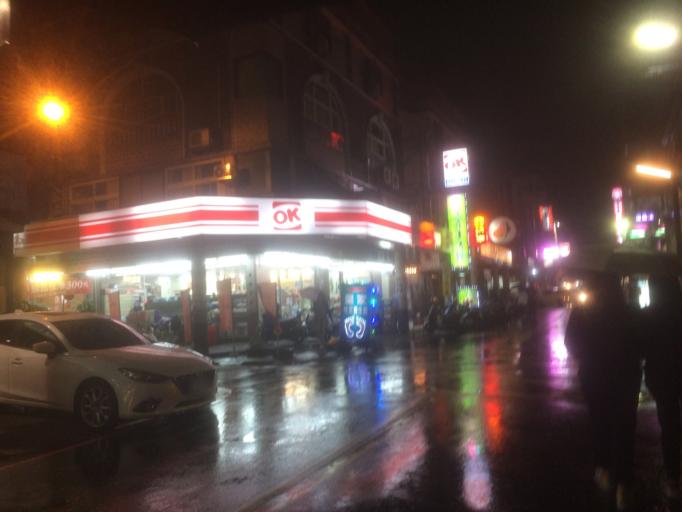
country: TW
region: Taiwan
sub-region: Yilan
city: Yilan
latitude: 24.6780
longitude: 121.7694
